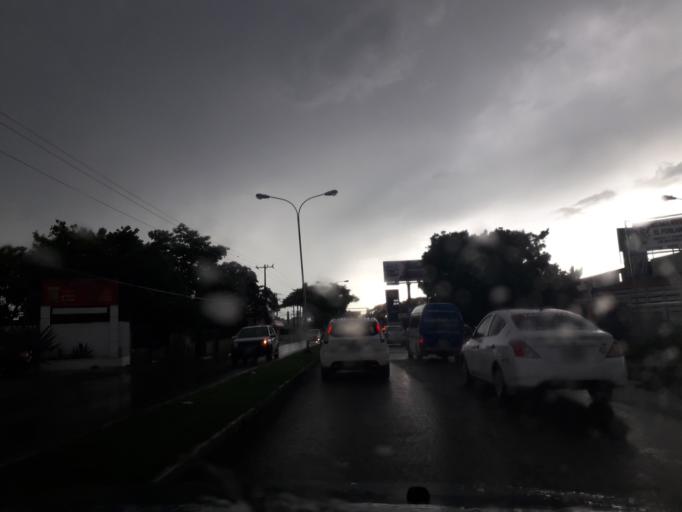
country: MX
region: Yucatan
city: Merida
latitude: 20.9790
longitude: -89.6463
